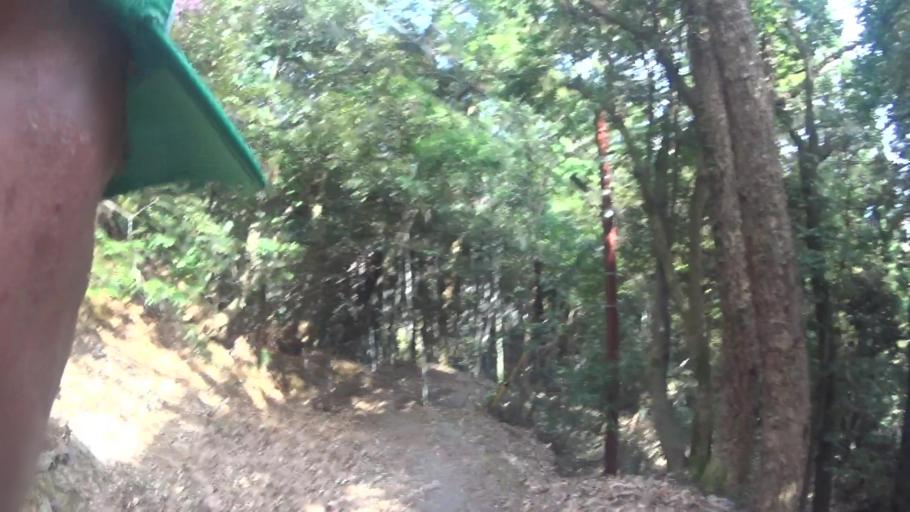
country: JP
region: Kyoto
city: Miyazu
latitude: 35.5843
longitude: 135.1947
